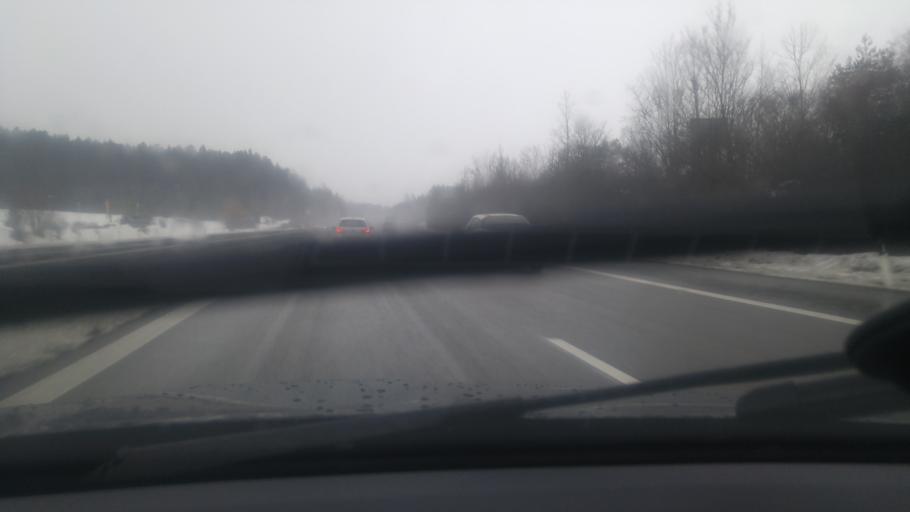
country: DE
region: Baden-Wuerttemberg
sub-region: Freiburg Region
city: Vohringen
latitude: 48.3138
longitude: 8.6435
